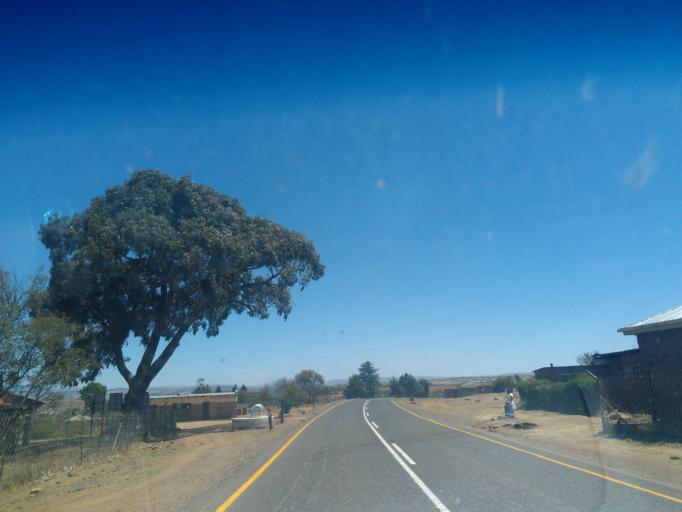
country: LS
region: Berea
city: Teyateyaneng
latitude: -29.2585
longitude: 27.7239
